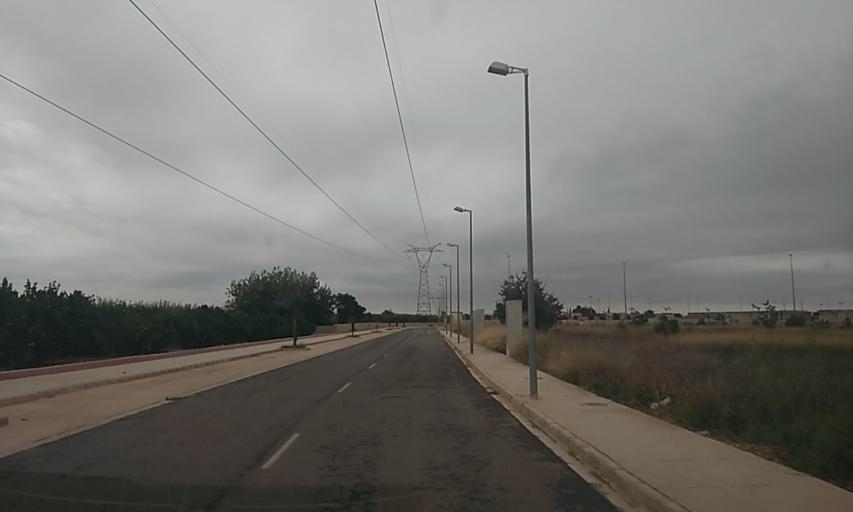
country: ES
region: Valencia
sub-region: Provincia de Valencia
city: L'Alcudia
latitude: 39.1916
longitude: -0.5174
